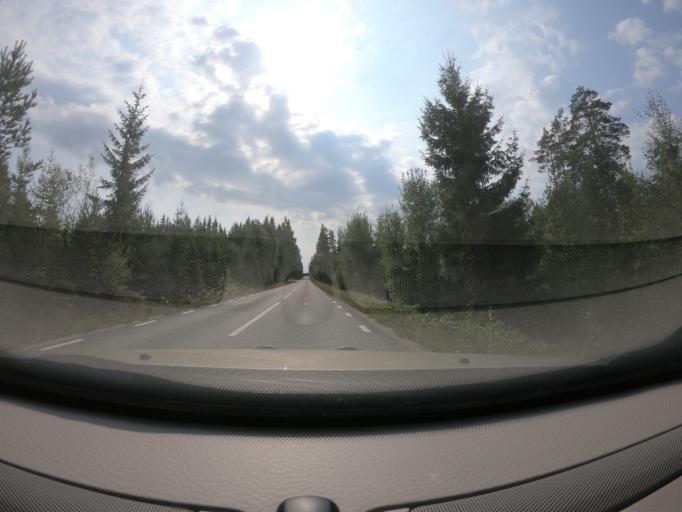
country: SE
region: Kronoberg
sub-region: Vaxjo Kommun
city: Braas
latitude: 57.1445
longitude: 14.9601
